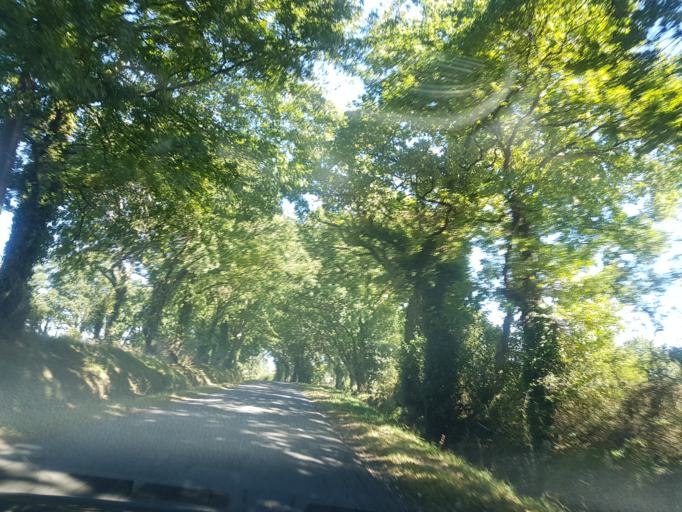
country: FR
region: Pays de la Loire
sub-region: Departement de la Loire-Atlantique
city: Mesquer
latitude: 47.3953
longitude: -2.4490
